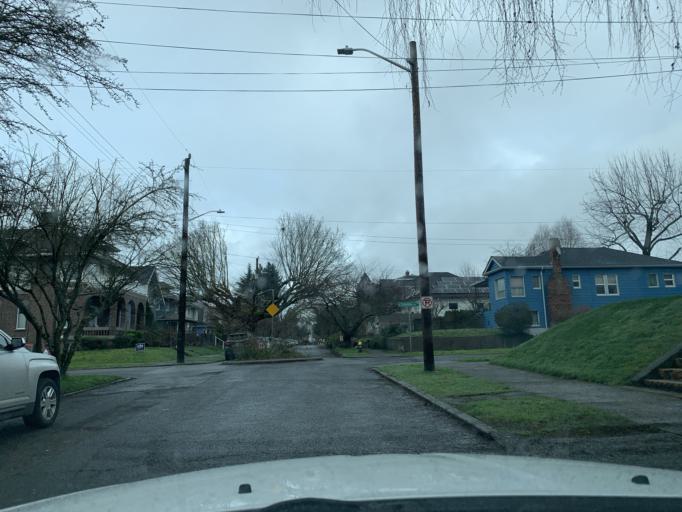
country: US
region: Washington
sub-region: King County
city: Seattle
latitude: 47.6090
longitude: -122.2915
